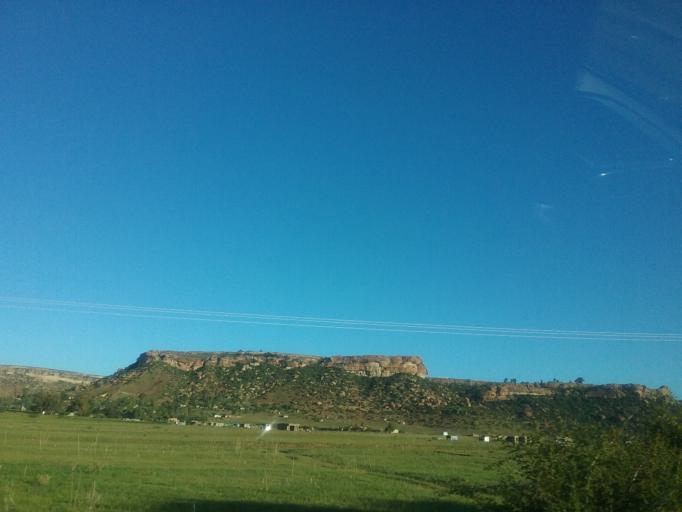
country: LS
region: Maseru
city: Maseru
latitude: -29.2624
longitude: 27.6025
